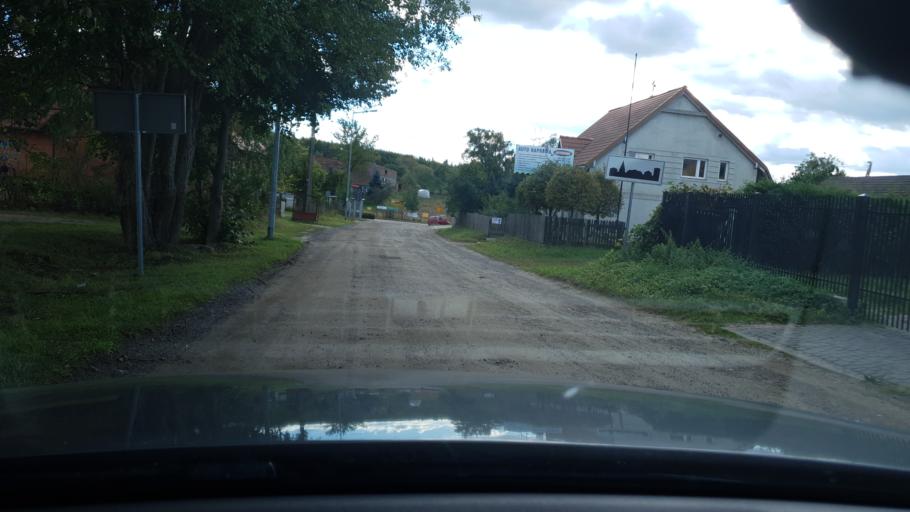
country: PL
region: Pomeranian Voivodeship
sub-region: Powiat wejherowski
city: Reda
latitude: 54.5750
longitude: 18.3092
